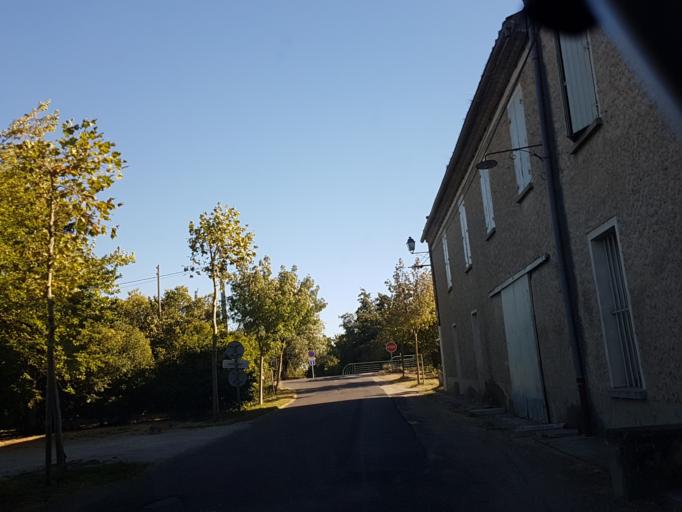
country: FR
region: Provence-Alpes-Cote d'Azur
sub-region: Departement du Vaucluse
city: Jonquerettes
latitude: 43.9603
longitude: 4.9406
